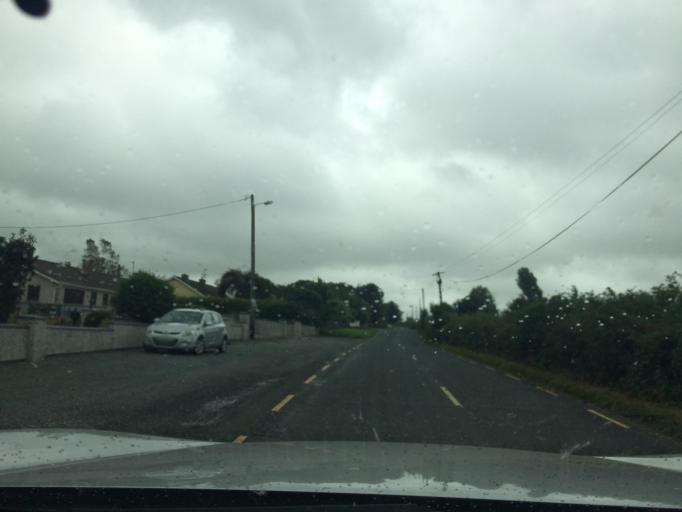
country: IE
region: Munster
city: Cashel
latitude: 52.5481
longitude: -7.8950
